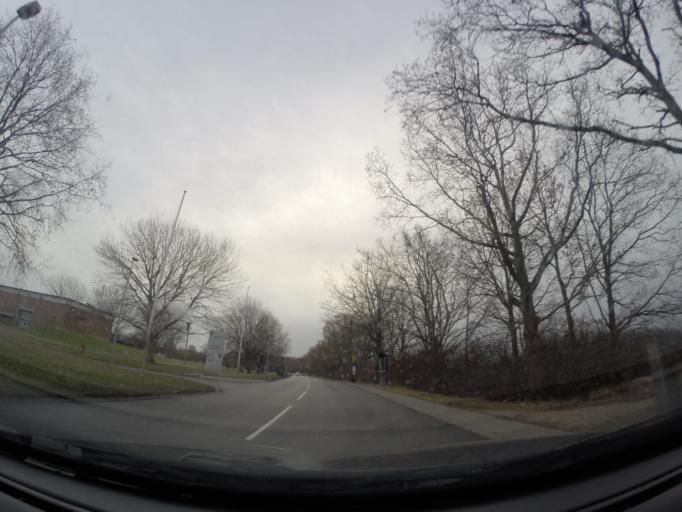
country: DK
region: Capital Region
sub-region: Hoje-Taastrup Kommune
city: Taastrup
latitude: 55.6596
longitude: 12.2691
